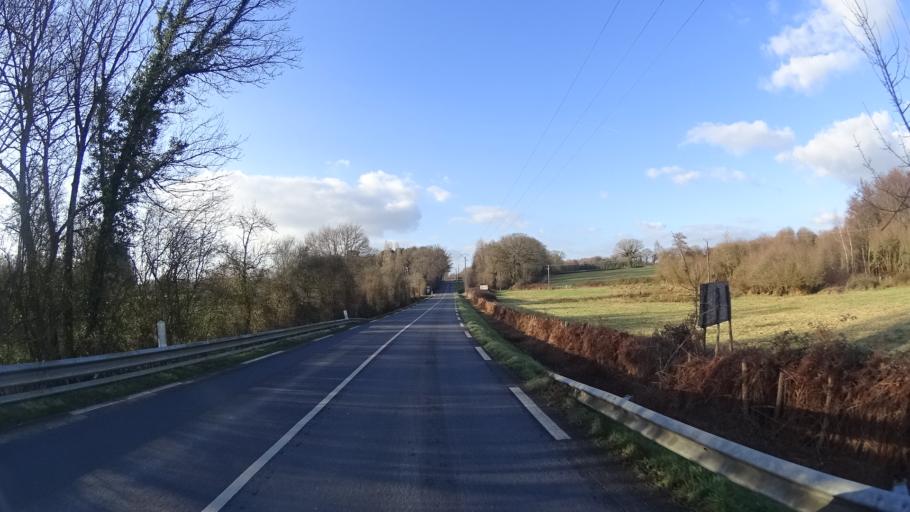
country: FR
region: Pays de la Loire
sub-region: Departement de la Loire-Atlantique
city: Plesse
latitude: 47.5319
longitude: -1.9155
